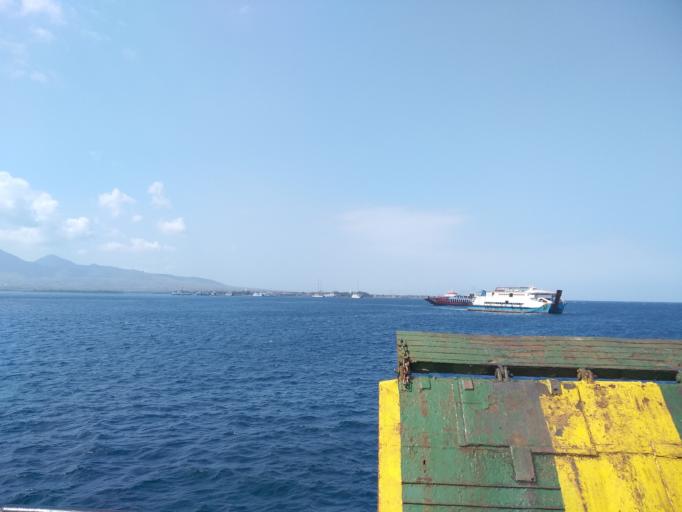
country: ID
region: Bali
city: Gilimanuk
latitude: -8.1476
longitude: 114.4316
